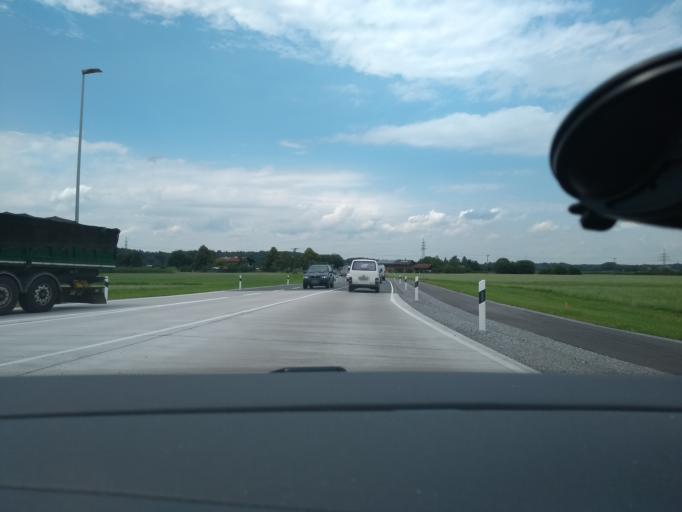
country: DE
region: Bavaria
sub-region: Upper Bavaria
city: Rosenheim
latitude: 47.8836
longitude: 12.1164
